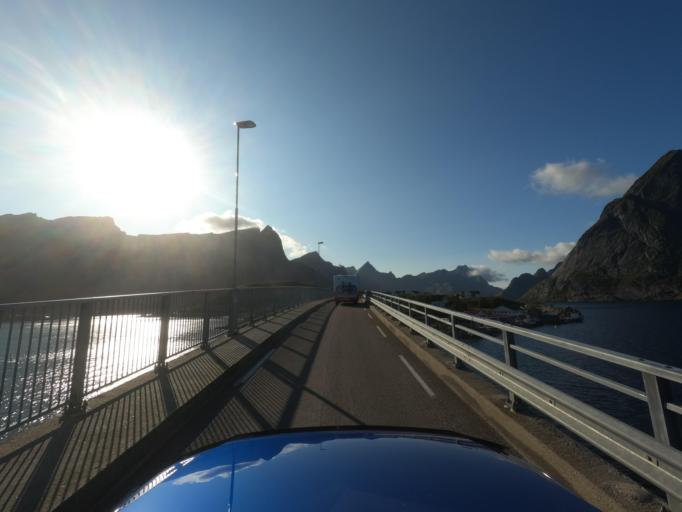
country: NO
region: Nordland
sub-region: Moskenes
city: Reine
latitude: 67.9419
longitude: 13.1081
